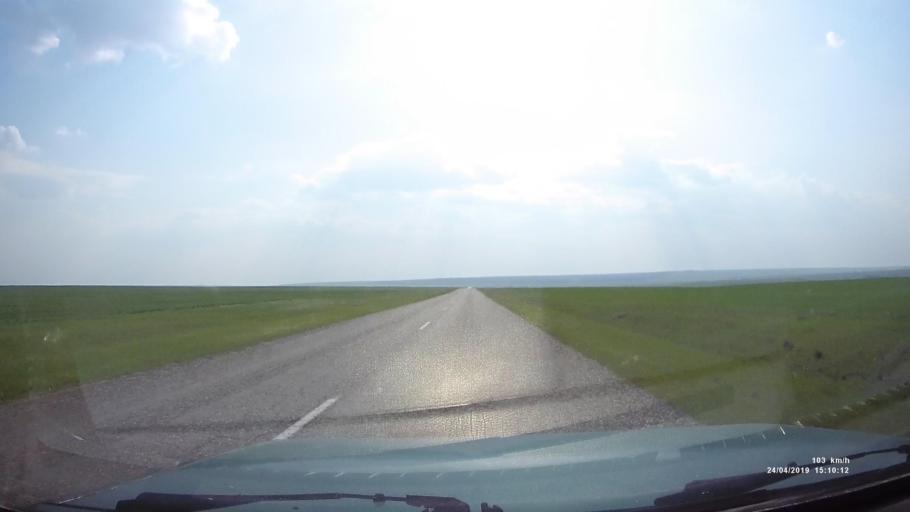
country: RU
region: Rostov
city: Remontnoye
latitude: 46.5517
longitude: 43.3459
